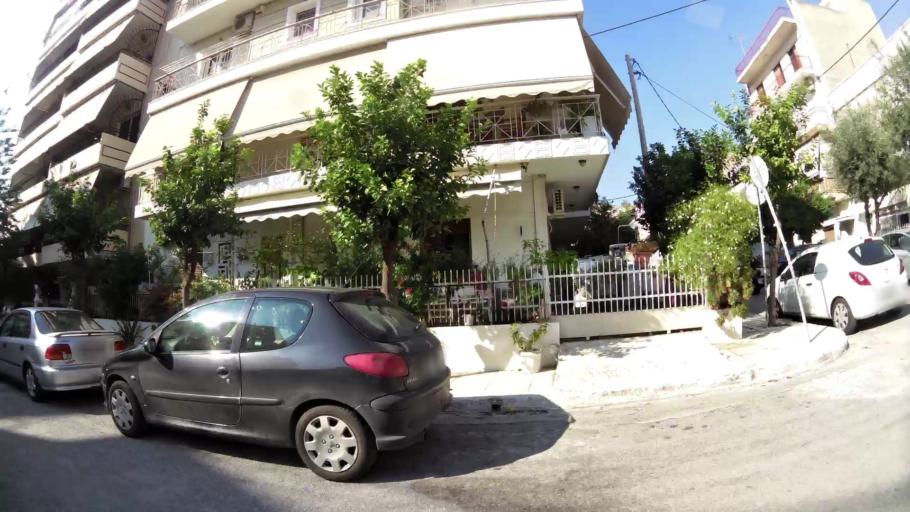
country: GR
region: Attica
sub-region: Nomos Piraios
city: Keratsini
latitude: 37.9652
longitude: 23.6193
